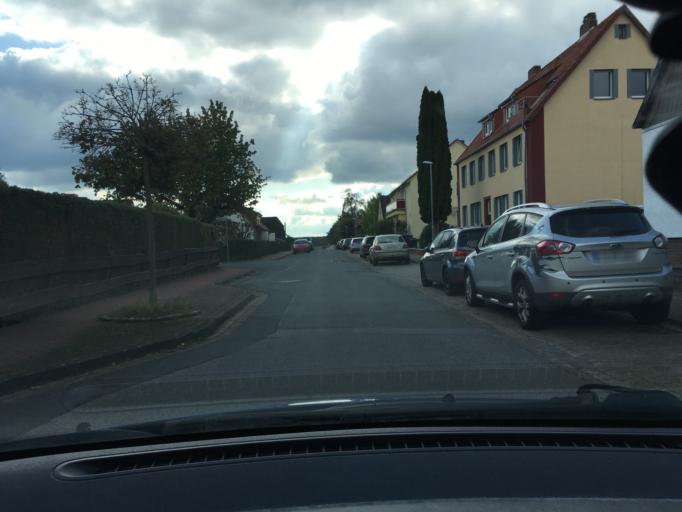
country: DE
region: Lower Saxony
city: Bad Munder am Deister
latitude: 52.1892
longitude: 9.4524
